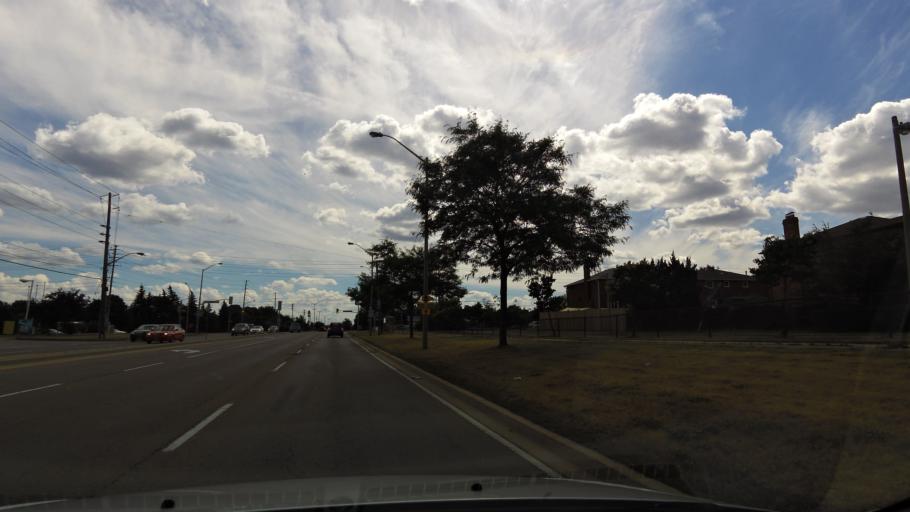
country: CA
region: Ontario
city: Oakville
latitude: 43.4759
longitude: -79.7012
